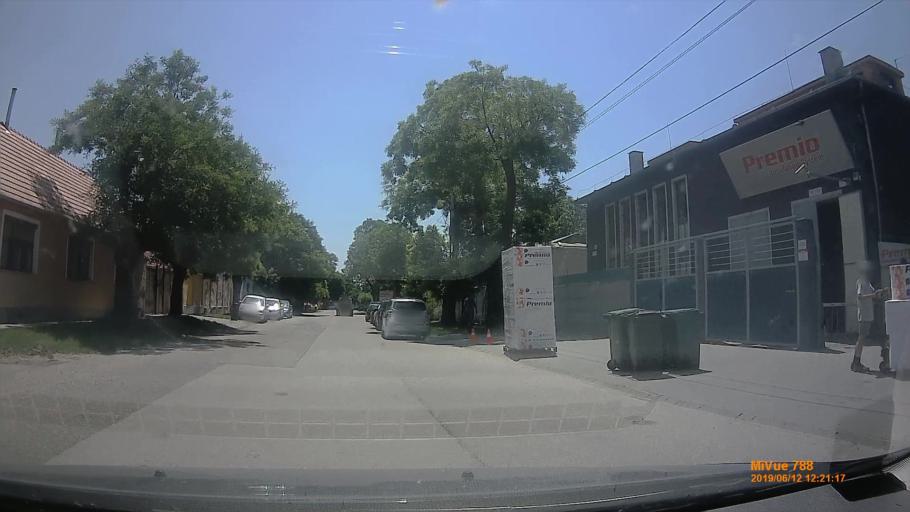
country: HU
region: Bacs-Kiskun
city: Kecskemet
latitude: 46.8986
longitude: 19.6921
